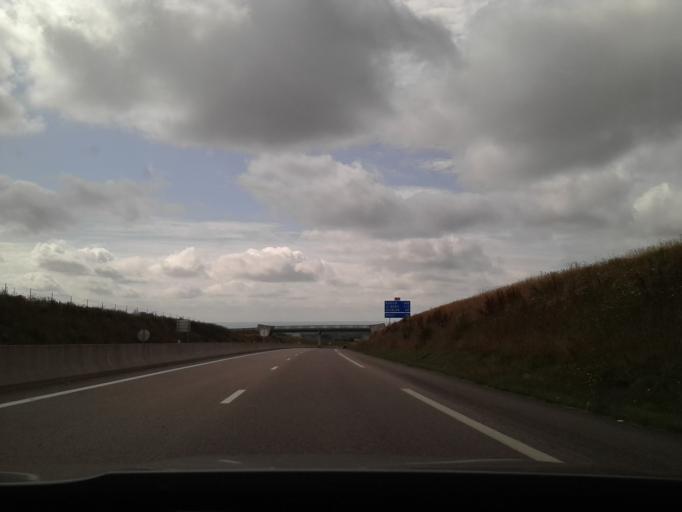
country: FR
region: Lower Normandy
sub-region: Departement de l'Orne
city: Courteilles
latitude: 48.8138
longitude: -0.1278
